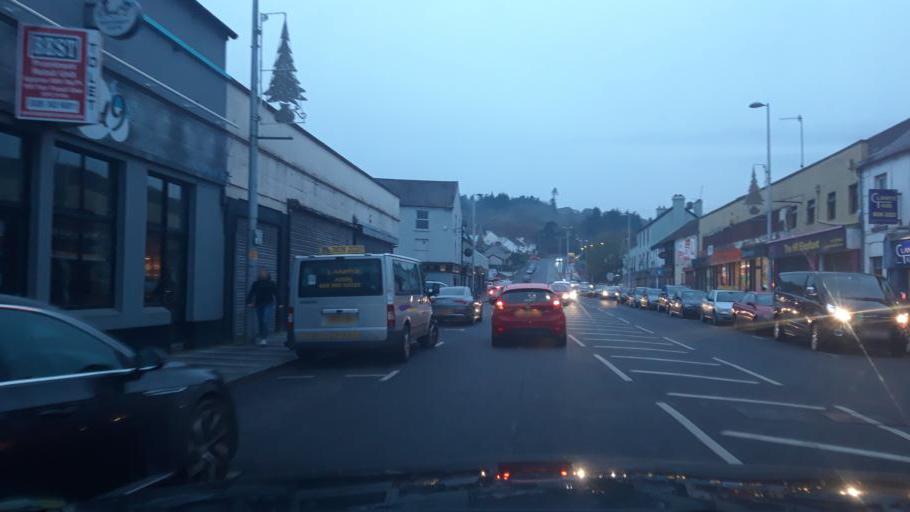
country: GB
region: Northern Ireland
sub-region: Newry and Mourne District
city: Newry
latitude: 54.1774
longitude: -6.3449
